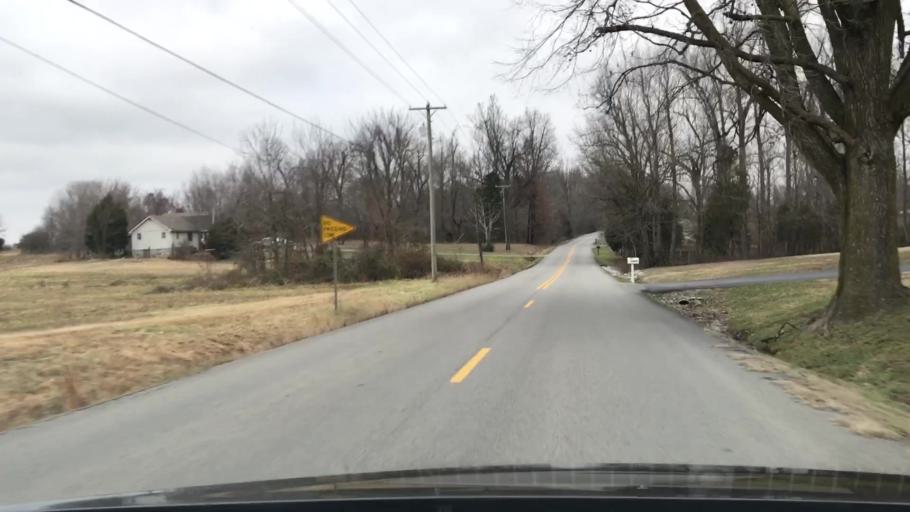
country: US
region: Kentucky
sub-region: Muhlenberg County
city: Morehead
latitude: 37.3616
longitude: -87.2335
